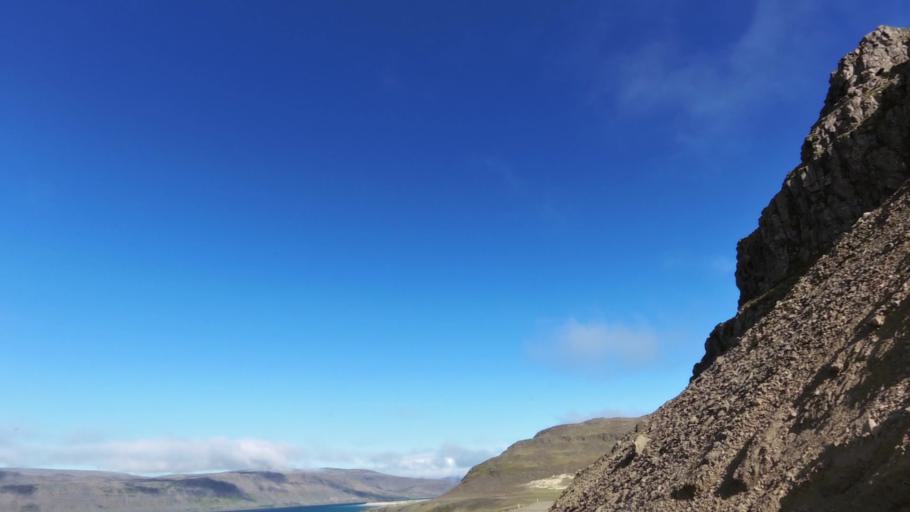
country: IS
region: West
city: Olafsvik
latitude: 65.5612
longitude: -24.0229
